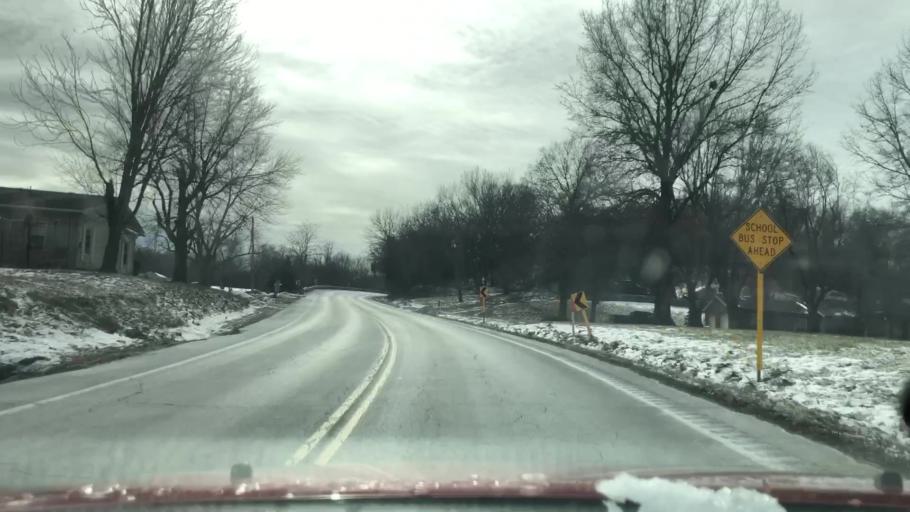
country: US
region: Missouri
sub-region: Jackson County
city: Oak Grove
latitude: 38.9397
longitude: -94.1327
